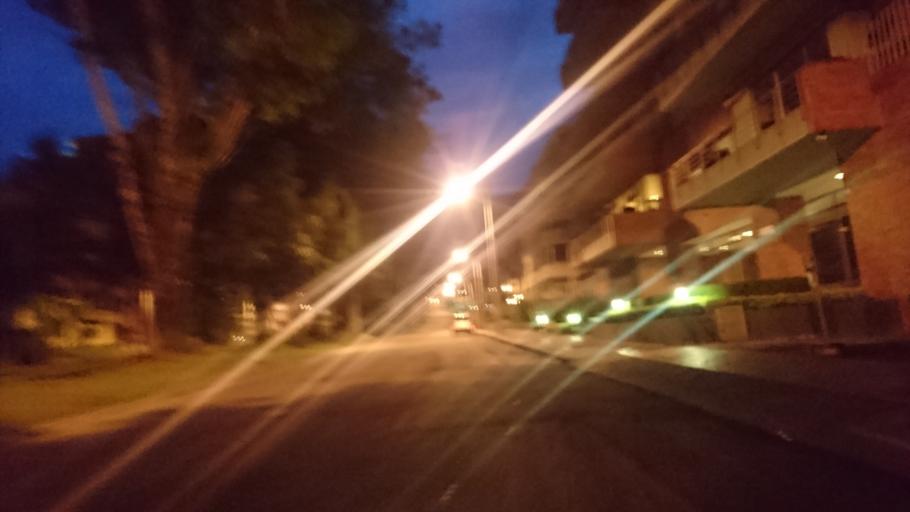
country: CO
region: Bogota D.C.
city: Barrio San Luis
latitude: 4.6726
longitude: -74.0464
